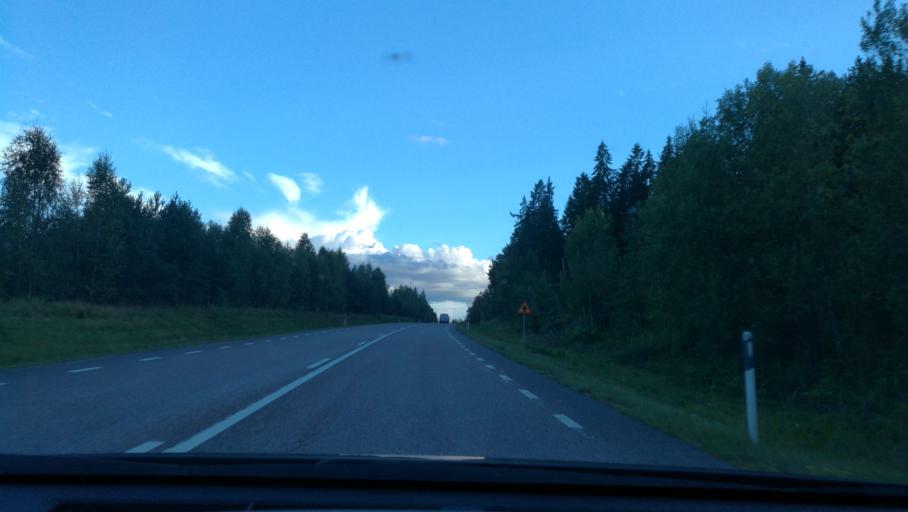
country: SE
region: Soedermanland
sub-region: Katrineholms Kommun
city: Katrineholm
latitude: 59.0432
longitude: 16.2195
